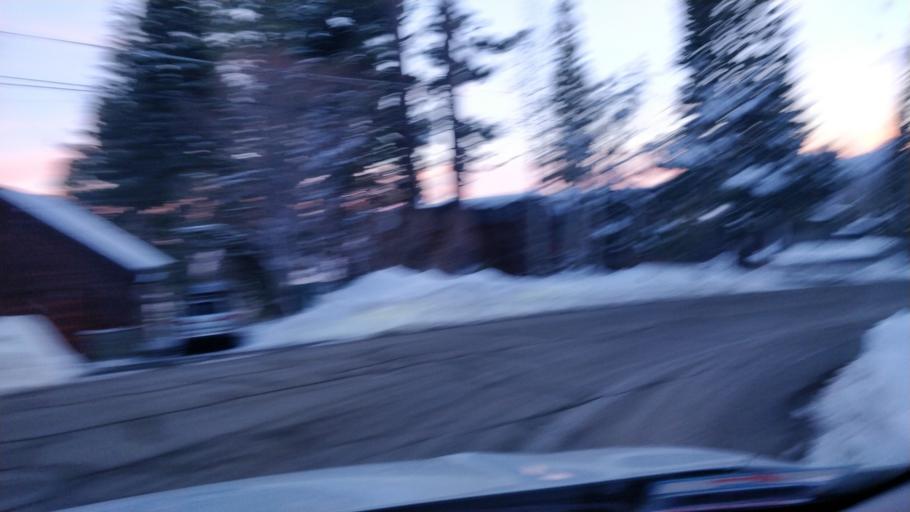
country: US
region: California
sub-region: Placer County
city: Sunnyside-Tahoe City
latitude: 39.1445
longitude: -120.1650
